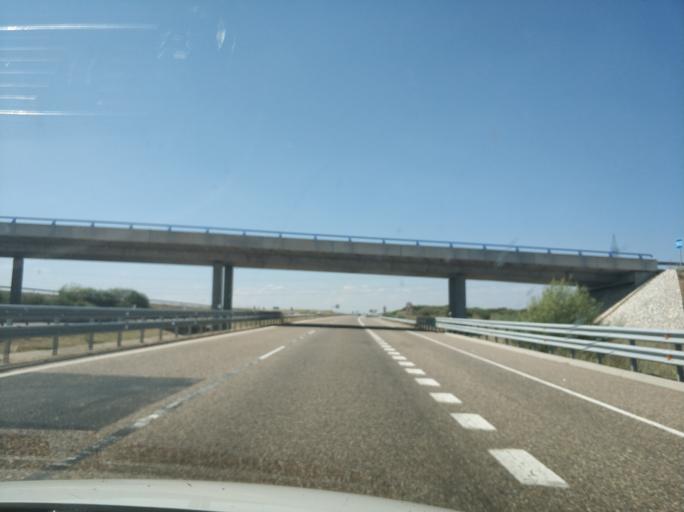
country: ES
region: Castille and Leon
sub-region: Provincia de Zamora
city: Roales
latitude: 41.5772
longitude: -5.7743
